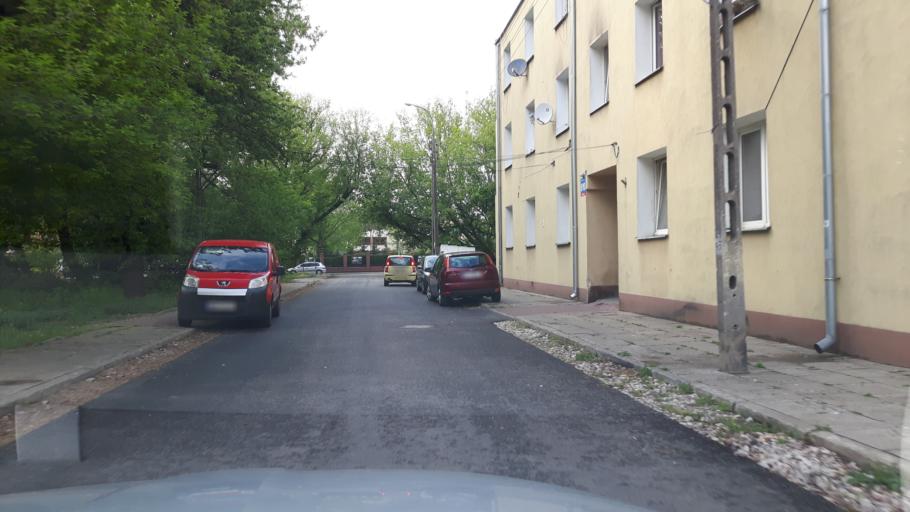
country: PL
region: Masovian Voivodeship
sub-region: Warszawa
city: Praga Poludnie
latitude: 52.2657
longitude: 21.0703
